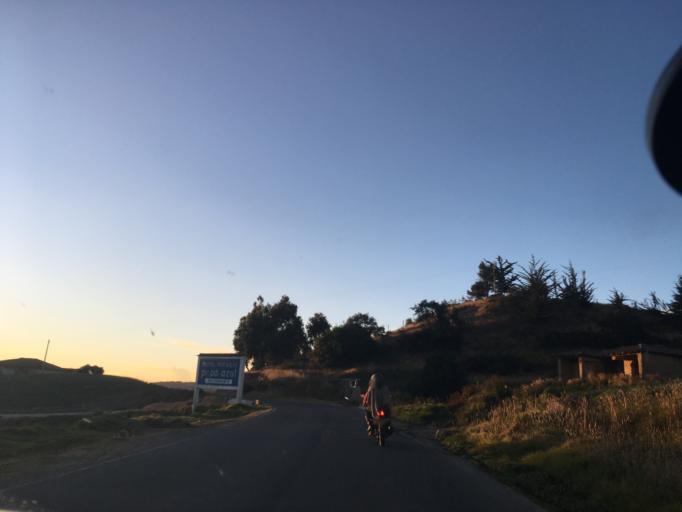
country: CO
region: Boyaca
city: Aquitania
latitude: 5.5707
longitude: -72.8924
